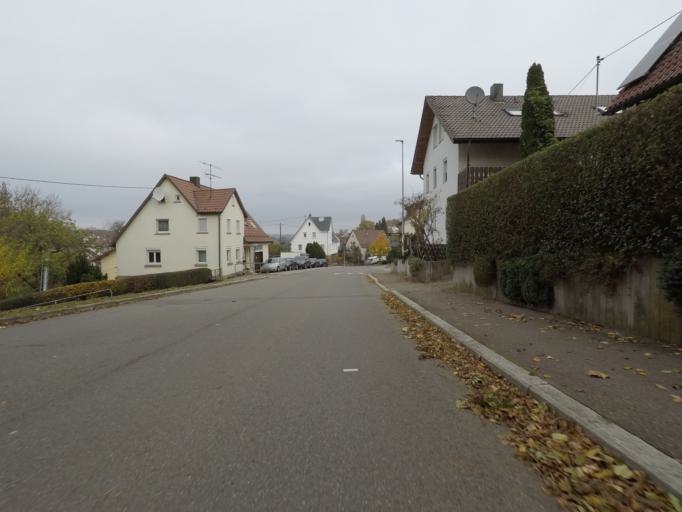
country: DE
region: Baden-Wuerttemberg
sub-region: Tuebingen Region
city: Reutlingen
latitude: 48.5171
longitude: 9.2332
